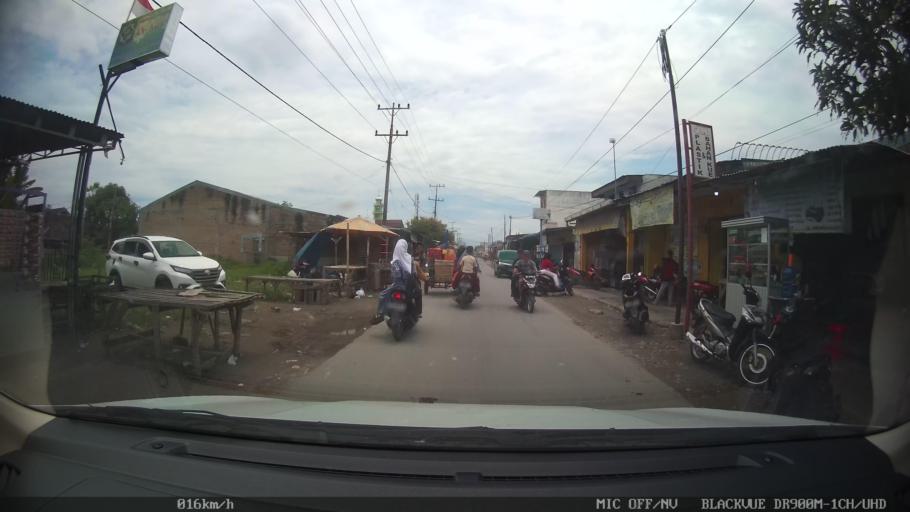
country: ID
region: North Sumatra
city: Sunggal
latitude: 3.6115
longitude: 98.5803
